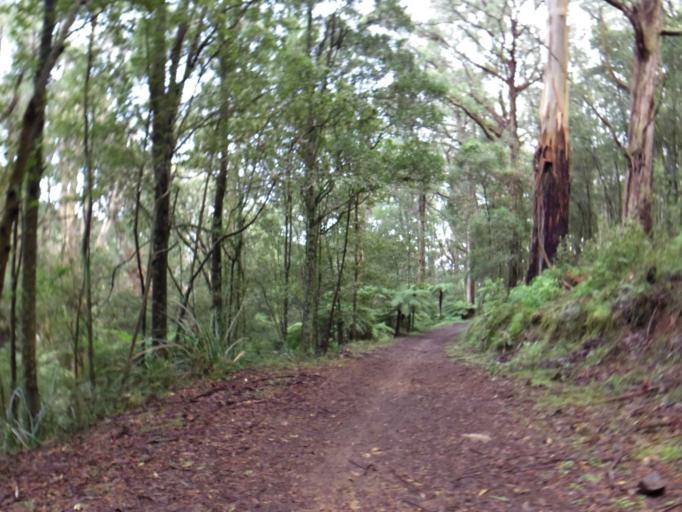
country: AU
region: Victoria
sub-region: Yarra Ranges
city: Olinda
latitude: -37.8486
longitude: 145.3524
